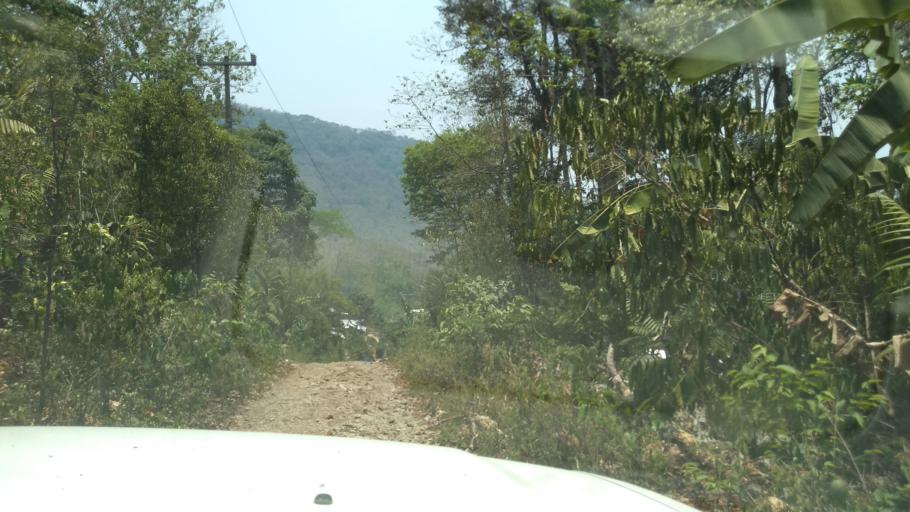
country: MX
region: Veracruz
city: Cosolapa
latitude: 18.5969
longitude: -96.7295
